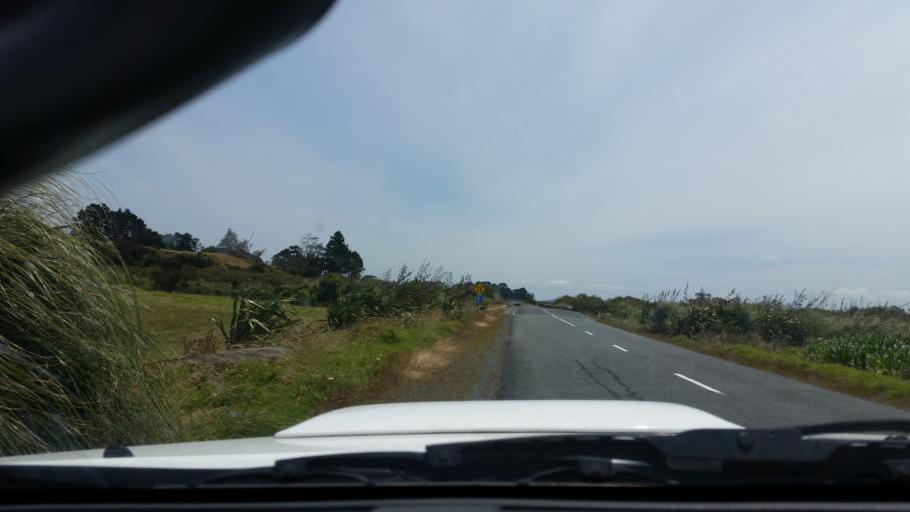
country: NZ
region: Northland
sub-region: Kaipara District
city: Dargaville
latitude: -36.1775
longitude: 174.0286
